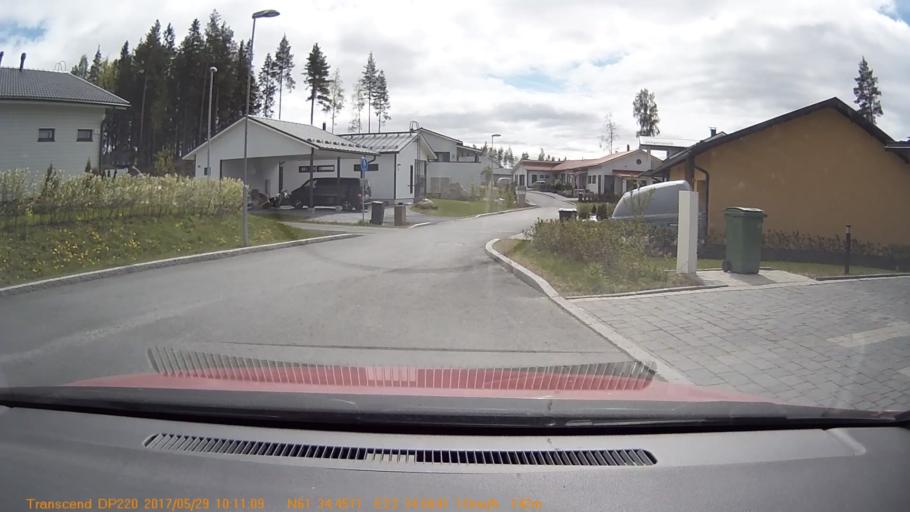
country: FI
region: Pirkanmaa
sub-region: Tampere
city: Yloejaervi
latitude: 61.5742
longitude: 23.5762
